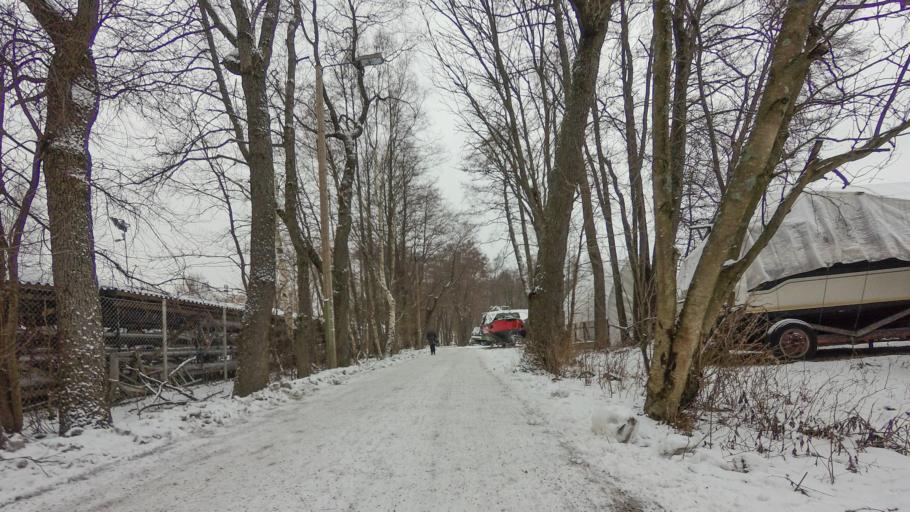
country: FI
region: Uusimaa
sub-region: Helsinki
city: Vantaa
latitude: 60.1971
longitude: 25.0643
